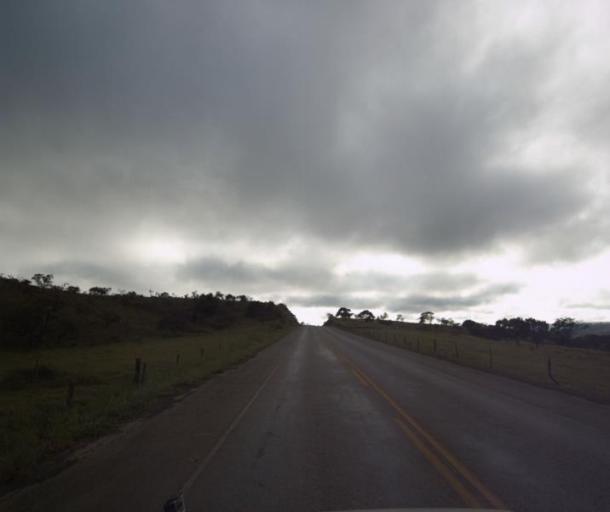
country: BR
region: Goias
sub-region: Pirenopolis
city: Pirenopolis
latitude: -15.7368
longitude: -48.7195
